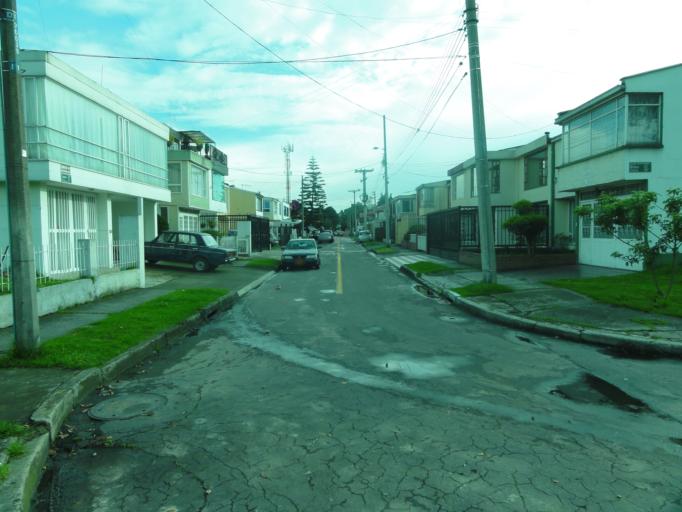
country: CO
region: Bogota D.C.
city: Bogota
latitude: 4.6540
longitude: -74.0847
